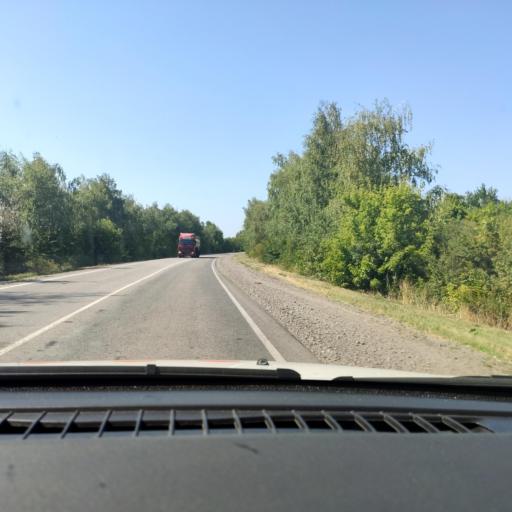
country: RU
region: Voronezj
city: Imeni Pervogo Maya
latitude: 50.7306
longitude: 39.3943
